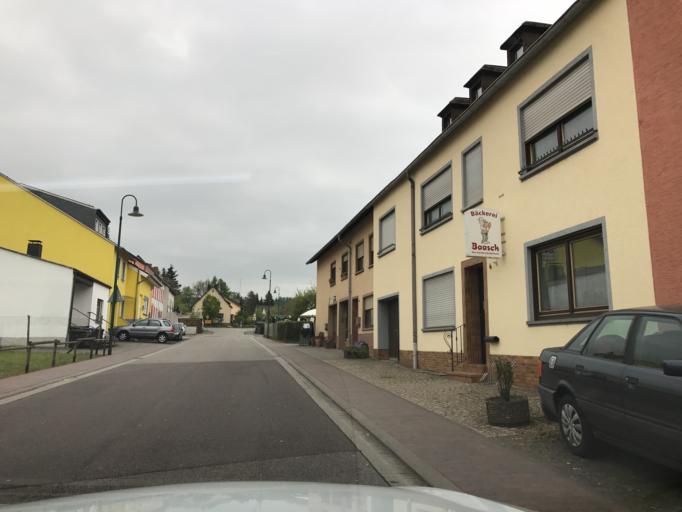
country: DE
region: Rheinland-Pfalz
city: Kanzem
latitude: 49.6668
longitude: 6.5758
